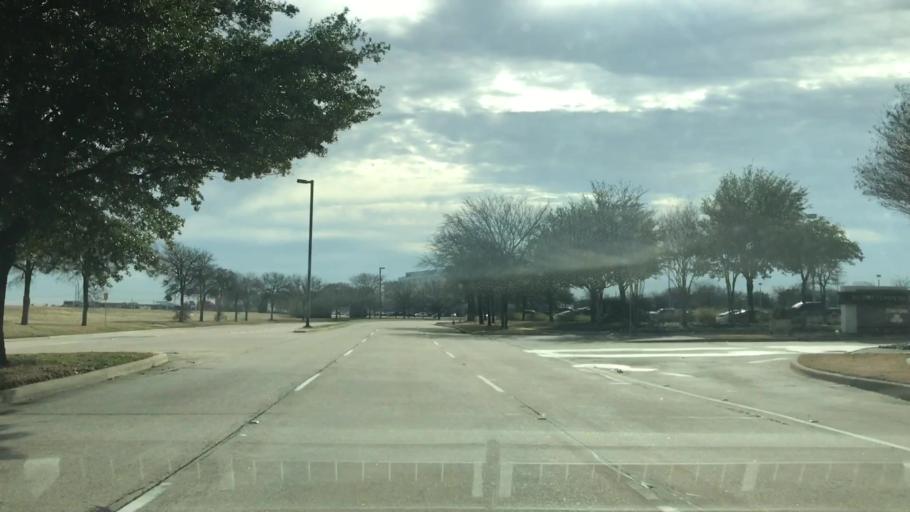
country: US
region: Texas
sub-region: Dallas County
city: Coppell
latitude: 32.9255
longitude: -97.0004
